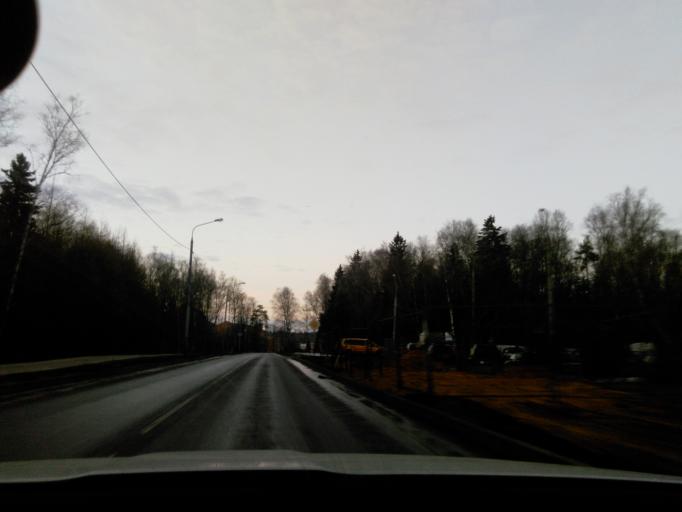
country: RU
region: Moscow
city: Zelenograd
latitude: 55.9954
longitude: 37.1812
